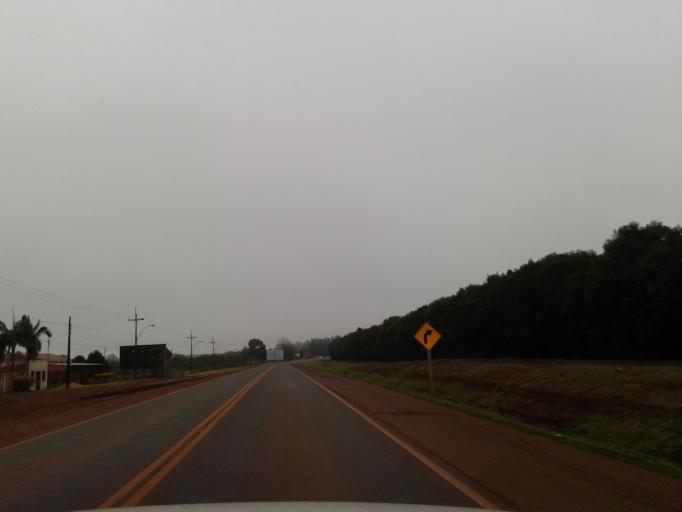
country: PY
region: Itapua
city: Pirapo
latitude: -26.8834
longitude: -55.4713
